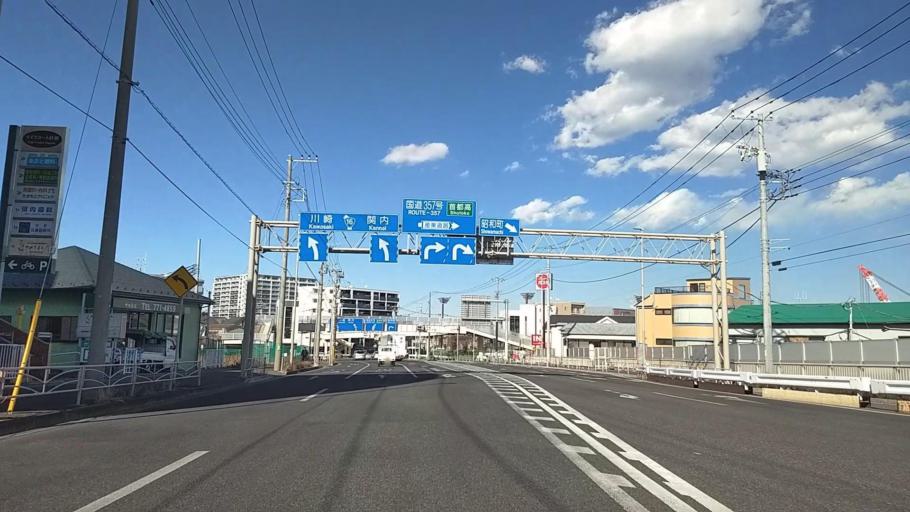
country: JP
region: Kanagawa
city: Yokohama
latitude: 35.3801
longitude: 139.6222
